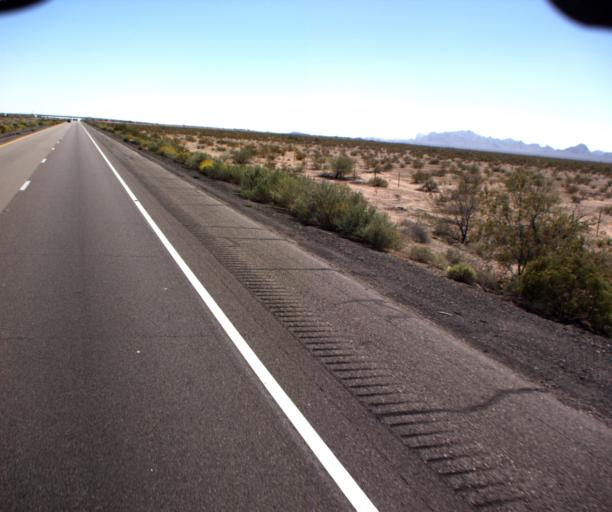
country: US
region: Arizona
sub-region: La Paz County
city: Salome
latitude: 33.5972
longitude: -113.5424
